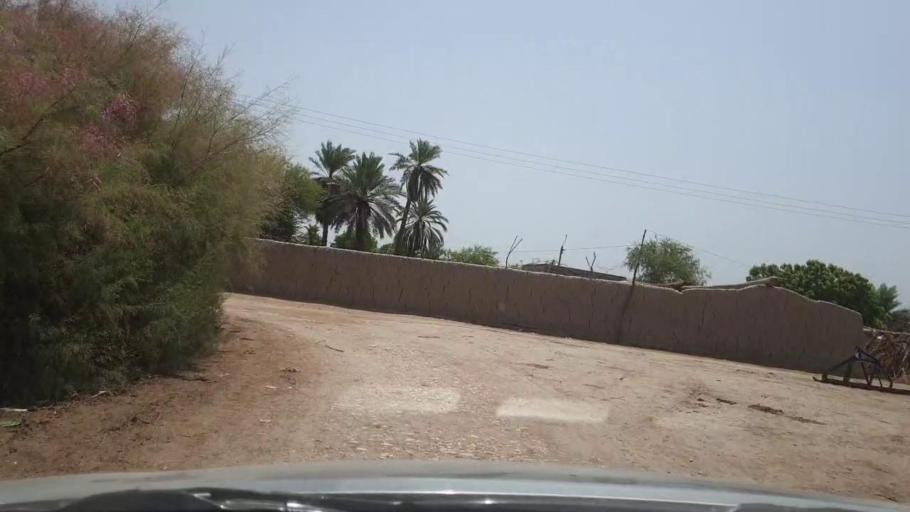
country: PK
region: Sindh
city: Pano Aqil
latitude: 27.8657
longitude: 69.1811
